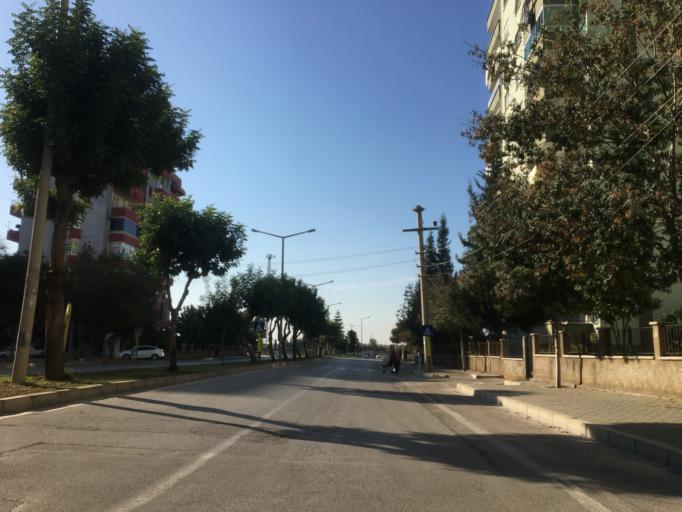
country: TR
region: Adana
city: Seyhan
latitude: 37.0283
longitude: 35.2566
